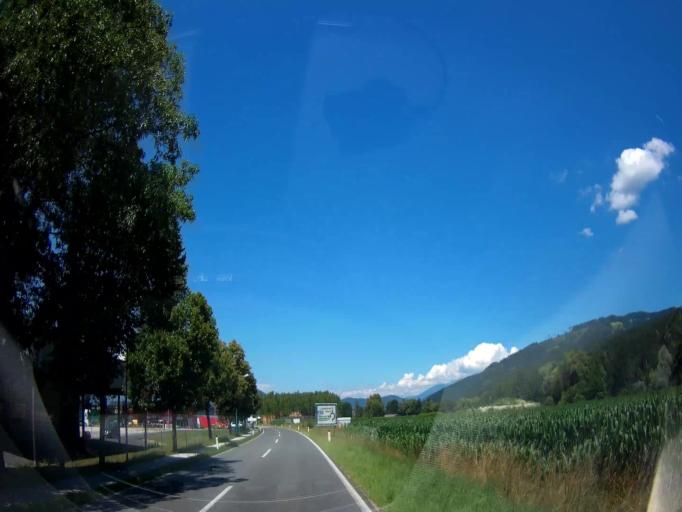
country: AT
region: Carinthia
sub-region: Politischer Bezirk Volkermarkt
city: Bleiburg/Pliberk
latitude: 46.5971
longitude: 14.7973
